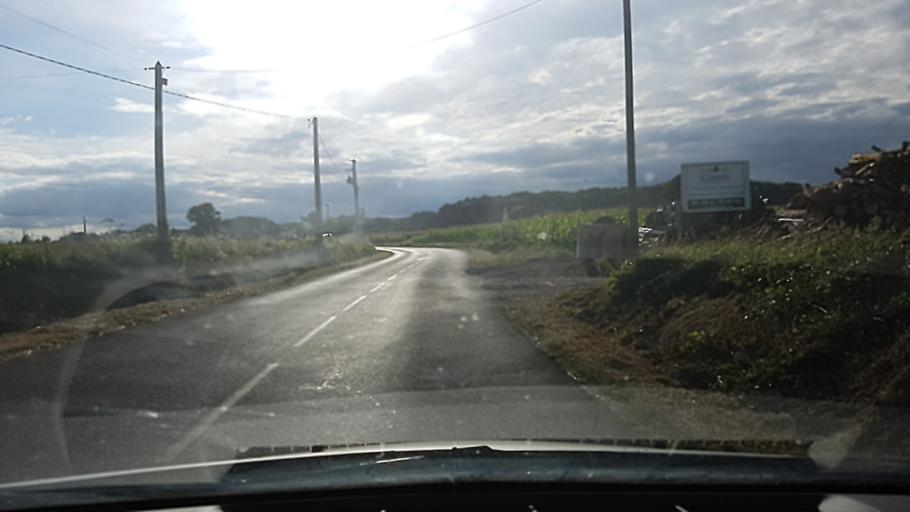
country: FR
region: Pays de la Loire
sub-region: Departement de Maine-et-Loire
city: Jarze
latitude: 47.5047
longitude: -0.2367
